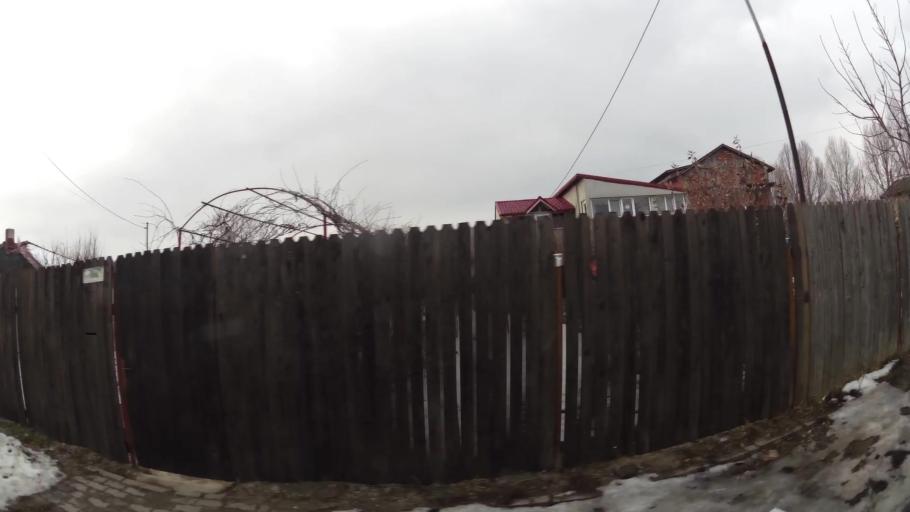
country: RO
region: Ilfov
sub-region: Voluntari City
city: Voluntari
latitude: 44.4903
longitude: 26.1639
